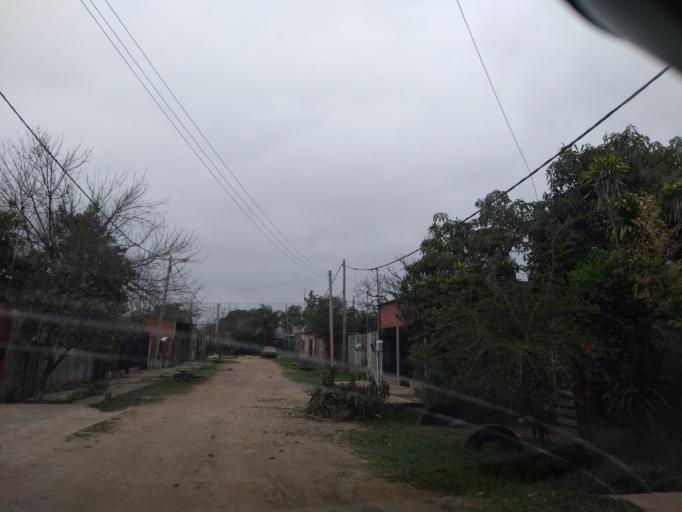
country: AR
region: Chaco
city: Resistencia
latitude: -27.4799
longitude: -58.9786
